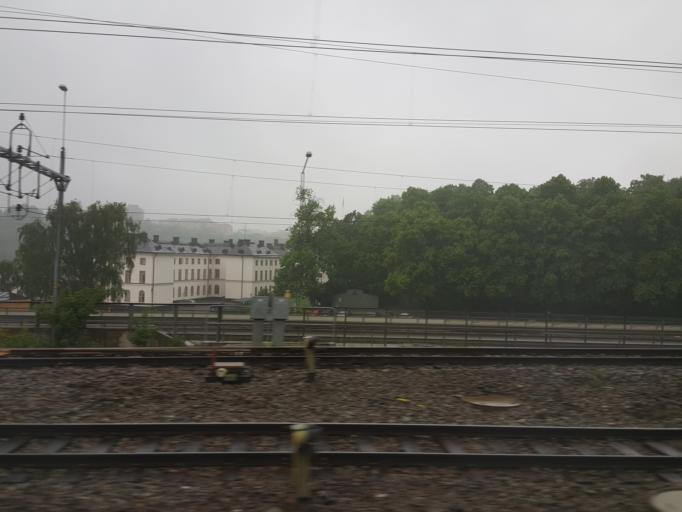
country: SE
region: Stockholm
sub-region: Solna Kommun
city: Solna
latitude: 59.3420
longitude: 18.0256
